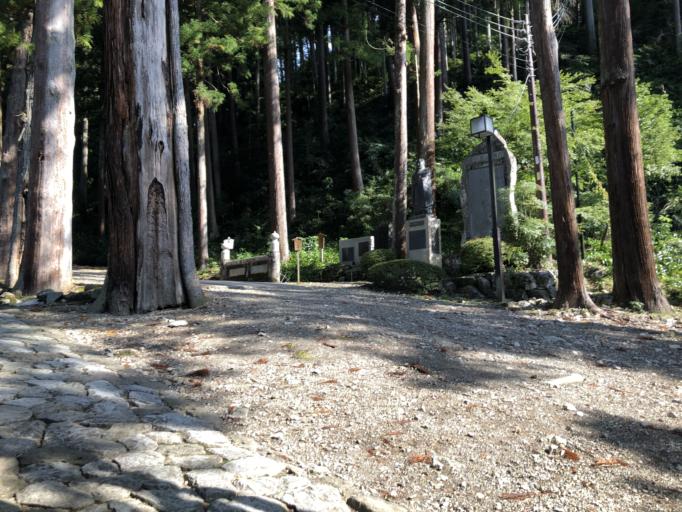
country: JP
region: Shizuoka
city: Fujinomiya
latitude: 35.3791
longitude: 138.4241
